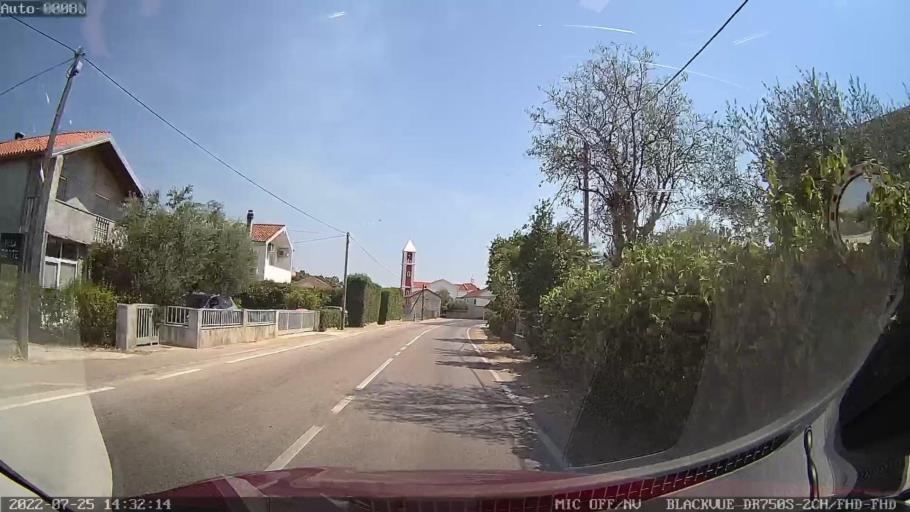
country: HR
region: Zadarska
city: Galovac
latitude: 44.1066
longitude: 15.3784
